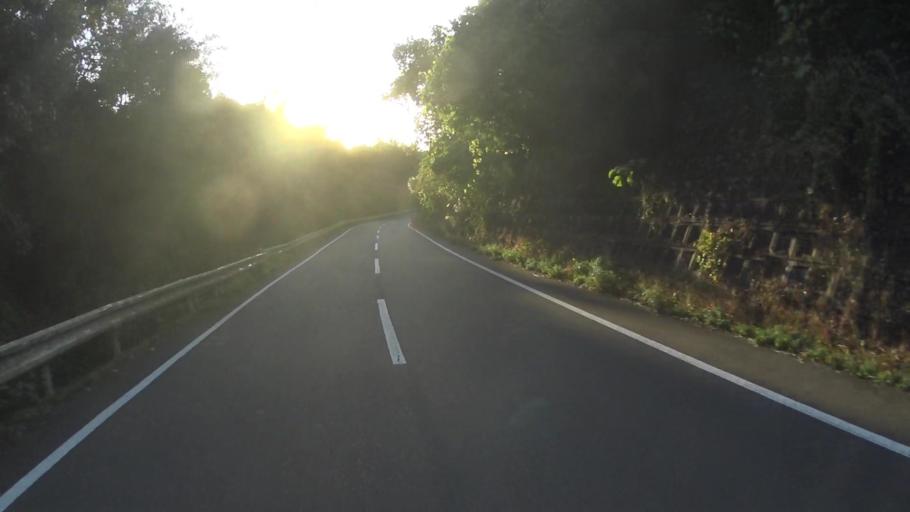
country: JP
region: Kyoto
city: Ayabe
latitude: 35.2251
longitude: 135.2370
